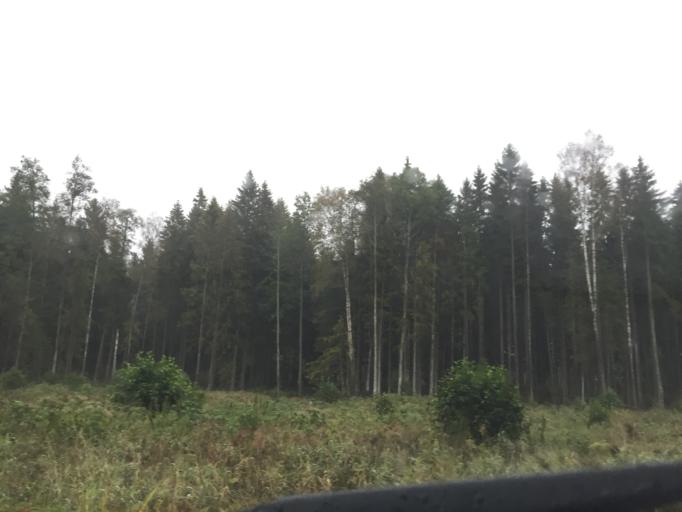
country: LV
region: Ropazu
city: Ropazi
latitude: 57.0092
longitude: 24.6811
